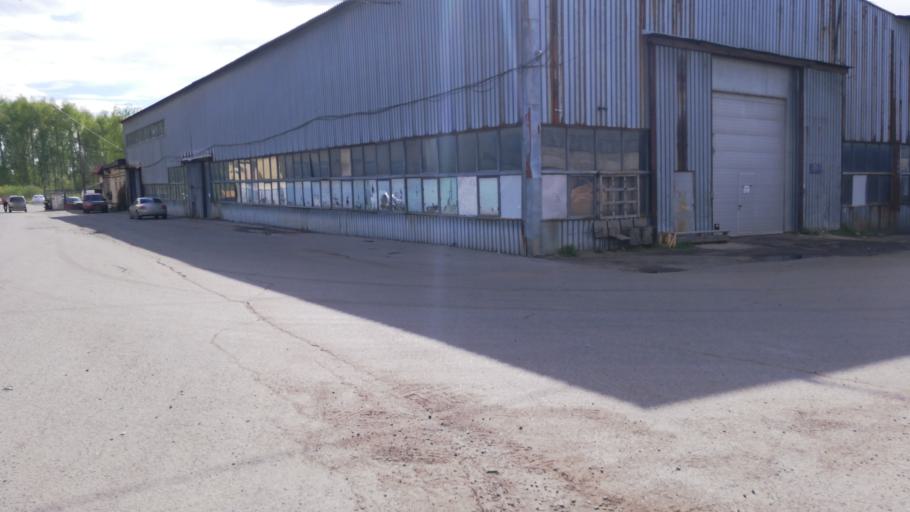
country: RU
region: Jaroslavl
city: Yaroslavl
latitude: 57.6246
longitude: 39.8204
